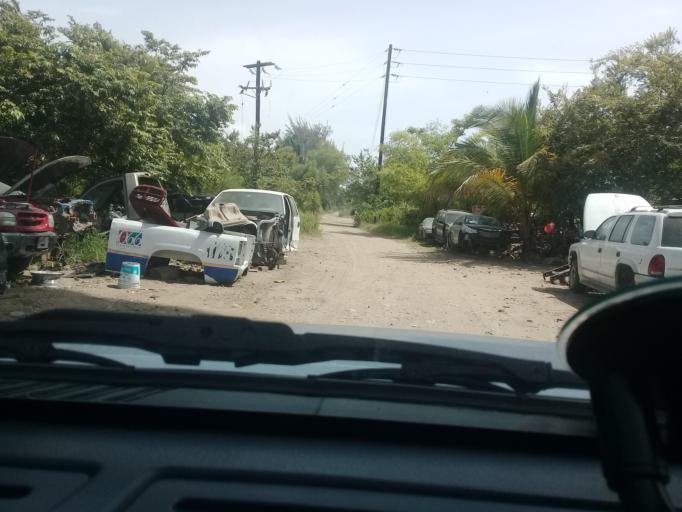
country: MX
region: Veracruz
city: Anahuac
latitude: 22.2258
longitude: -97.8335
